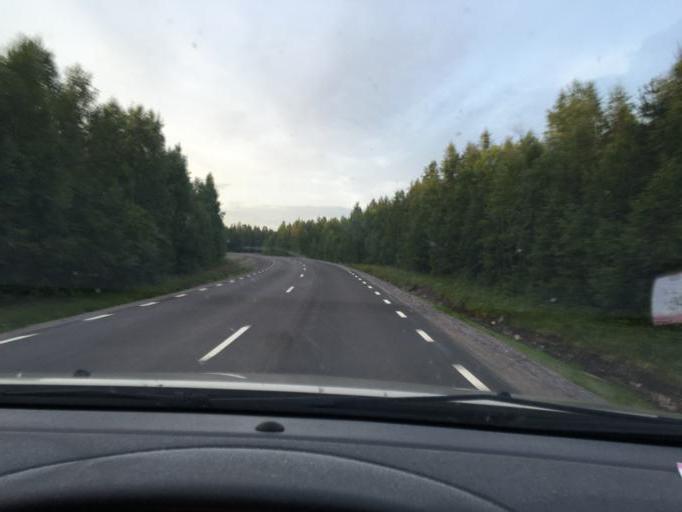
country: SE
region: Norrbotten
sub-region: Lulea Kommun
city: Ranea
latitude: 66.0499
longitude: 22.2094
